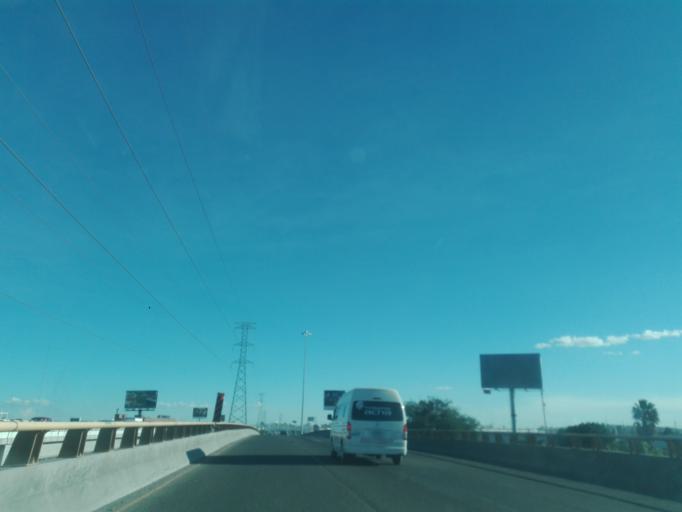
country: MX
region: Guanajuato
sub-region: Leon
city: Medina
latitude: 21.1144
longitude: -101.6258
